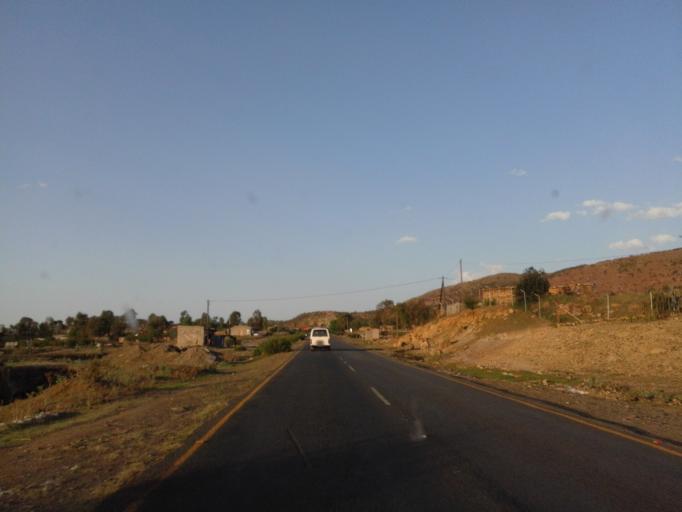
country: LS
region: Mafeteng
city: Mafeteng
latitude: -29.8437
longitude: 27.2303
